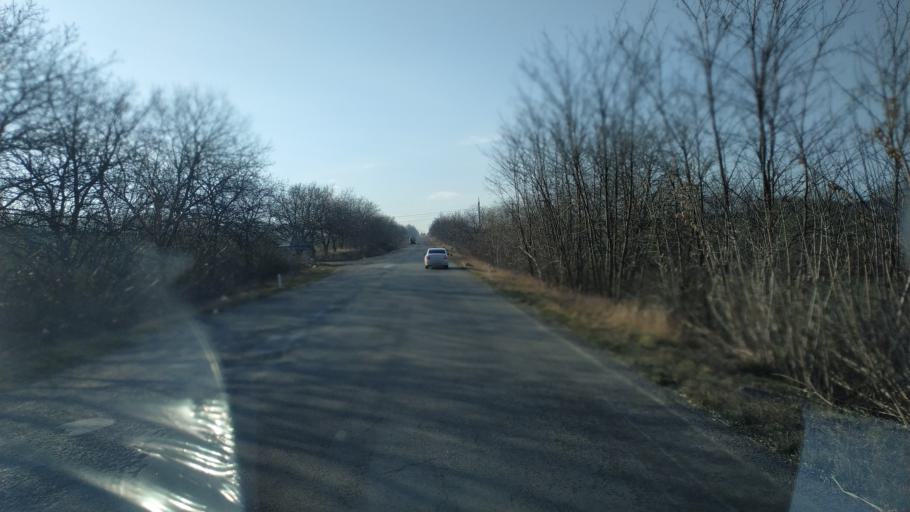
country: MD
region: Chisinau
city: Singera
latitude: 46.8780
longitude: 29.0395
